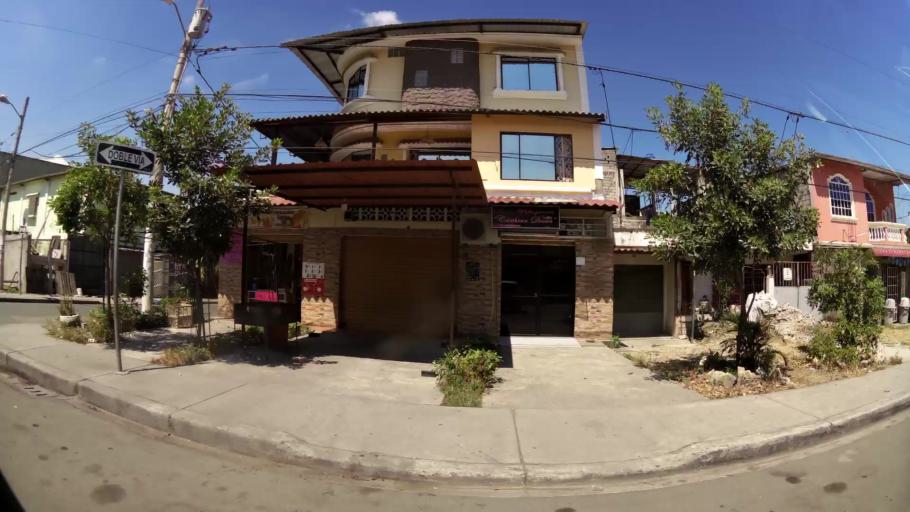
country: EC
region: Guayas
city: Guayaquil
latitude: -2.1908
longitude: -79.9447
